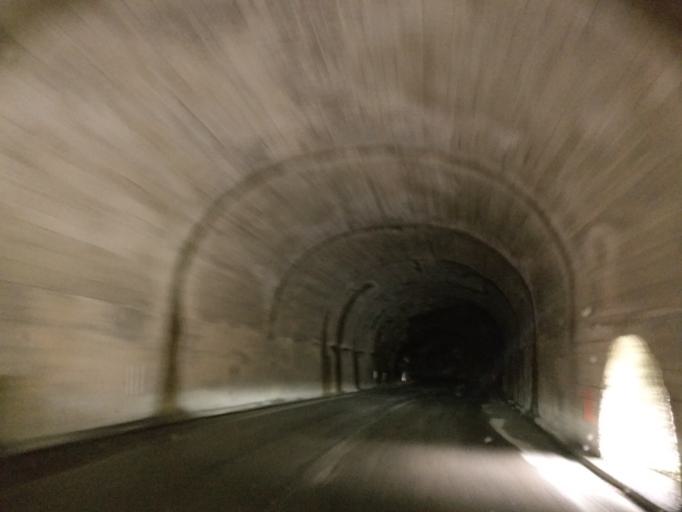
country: ME
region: Opstina Pluzine
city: Pluzine
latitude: 43.2577
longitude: 18.8450
